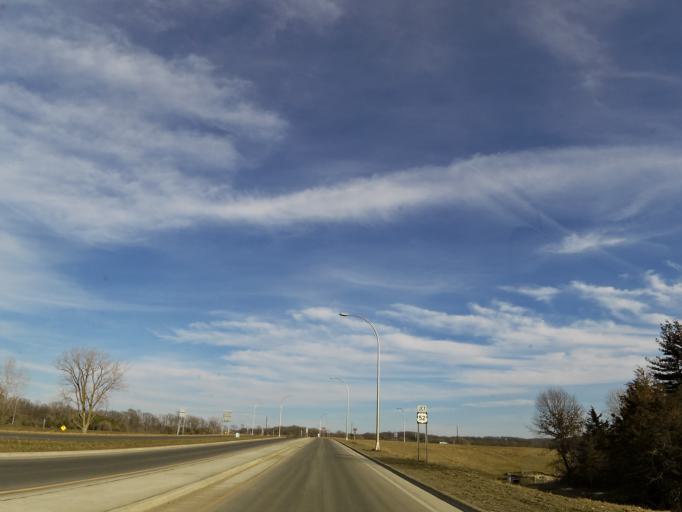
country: US
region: Minnesota
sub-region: Goodhue County
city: Cannon Falls
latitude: 44.4825
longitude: -92.9111
